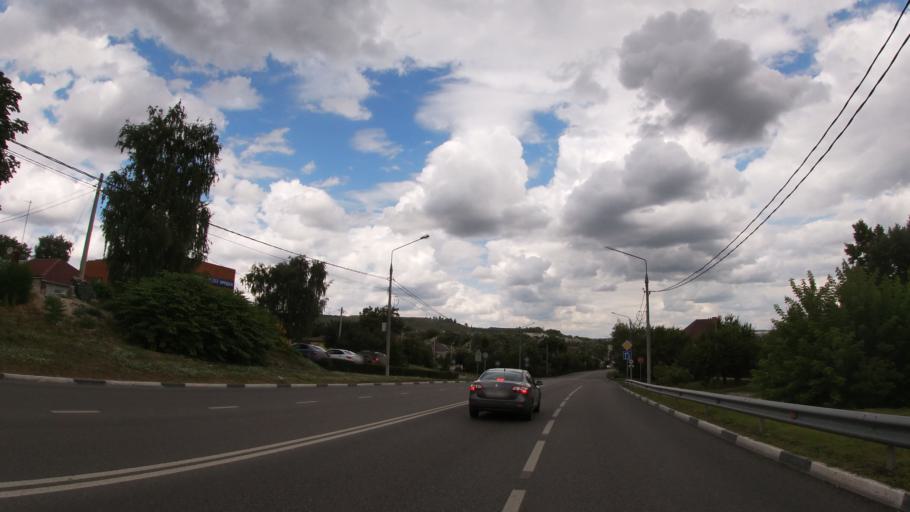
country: RU
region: Belgorod
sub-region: Belgorodskiy Rayon
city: Belgorod
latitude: 50.6051
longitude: 36.6109
